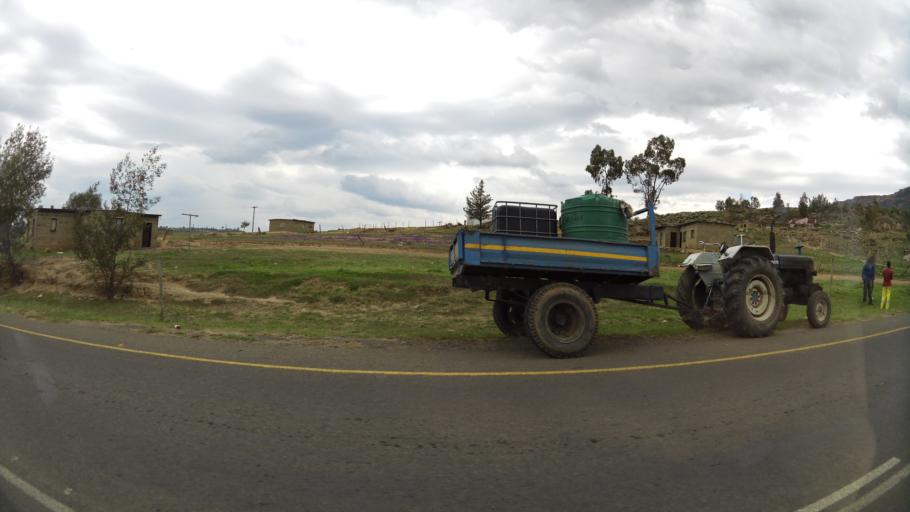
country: LS
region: Maseru
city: Maseru
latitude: -29.4025
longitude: 27.4744
